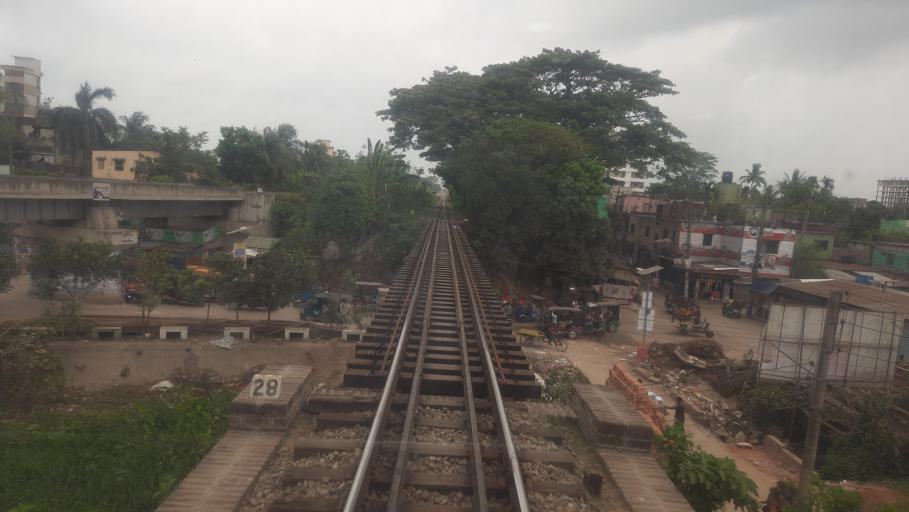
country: BD
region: Dhaka
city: Bhairab Bazar
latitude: 24.0506
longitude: 90.9875
